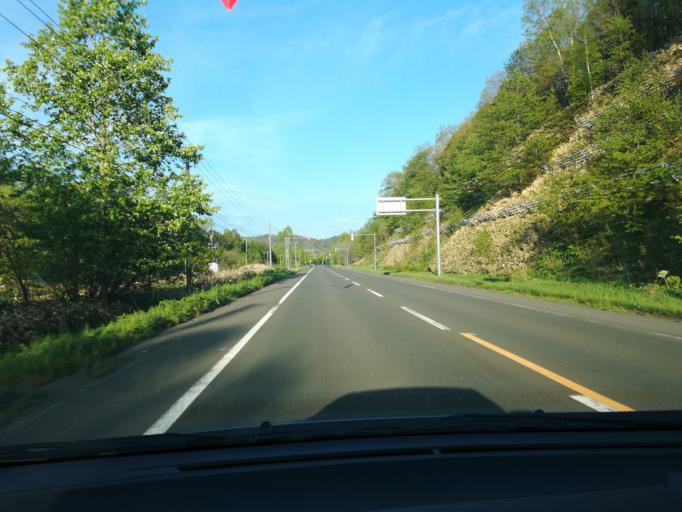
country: JP
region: Hokkaido
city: Shimo-furano
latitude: 43.1358
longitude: 142.6393
